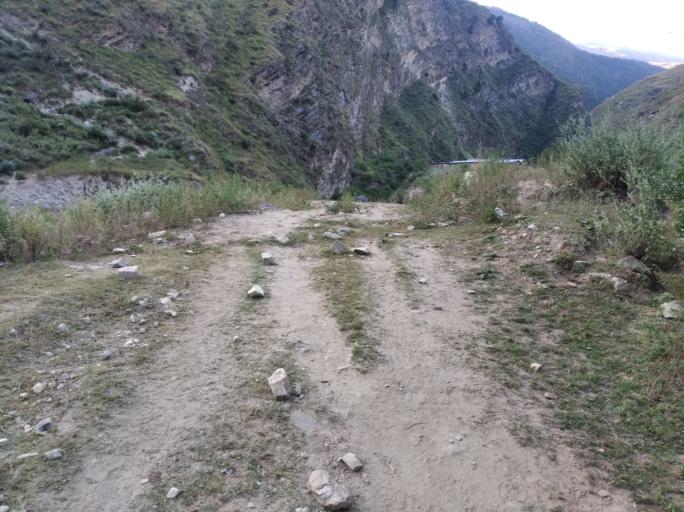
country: NP
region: Western Region
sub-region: Dhawalagiri Zone
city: Jomsom
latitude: 28.8798
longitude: 82.9908
